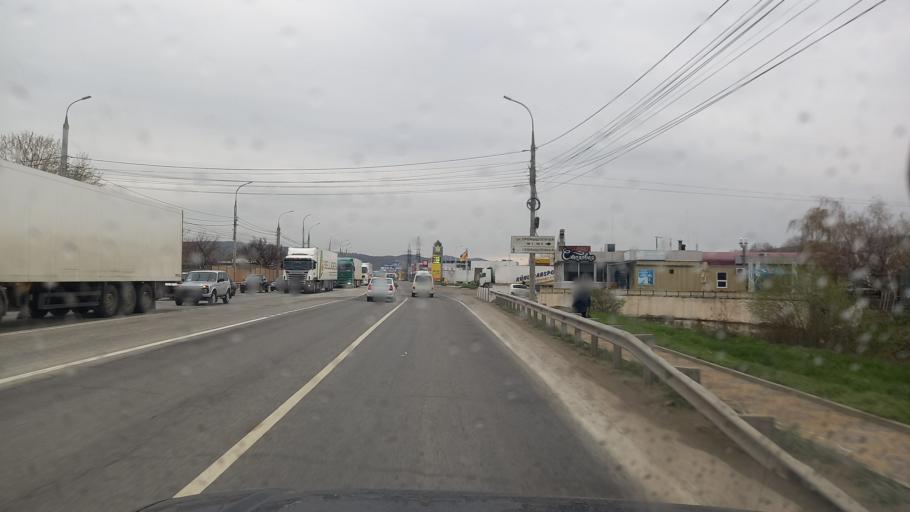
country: RU
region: Krasnodarskiy
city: Gayduk
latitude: 44.7657
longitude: 37.7134
